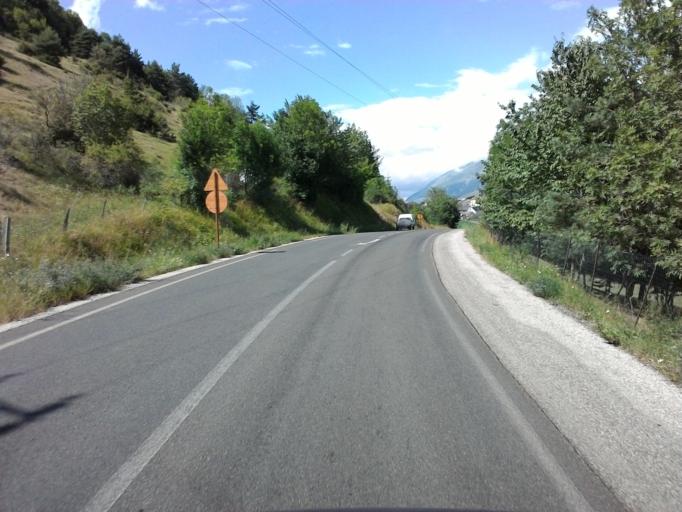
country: FR
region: Rhone-Alpes
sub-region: Departement de l'Isere
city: La Mure
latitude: 44.9027
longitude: 5.7813
